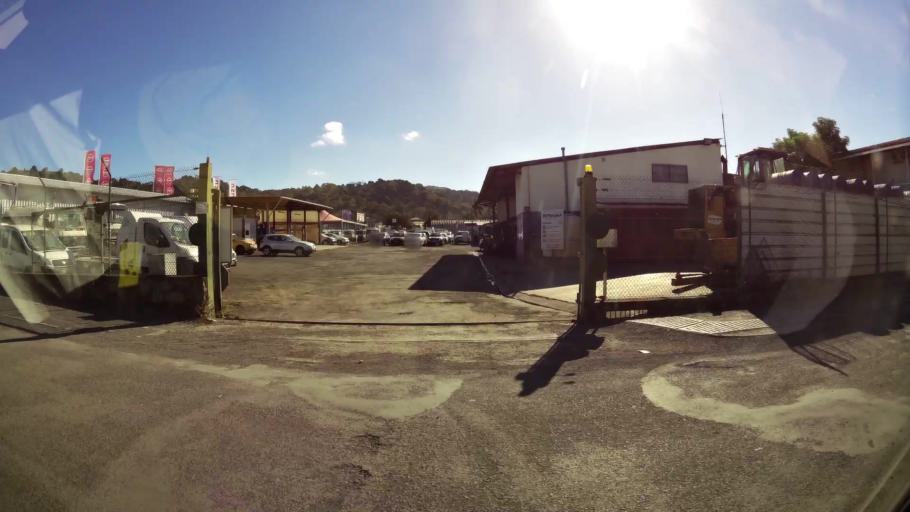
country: YT
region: Mamoudzou
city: Mamoudzou
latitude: -12.7712
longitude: 45.2253
